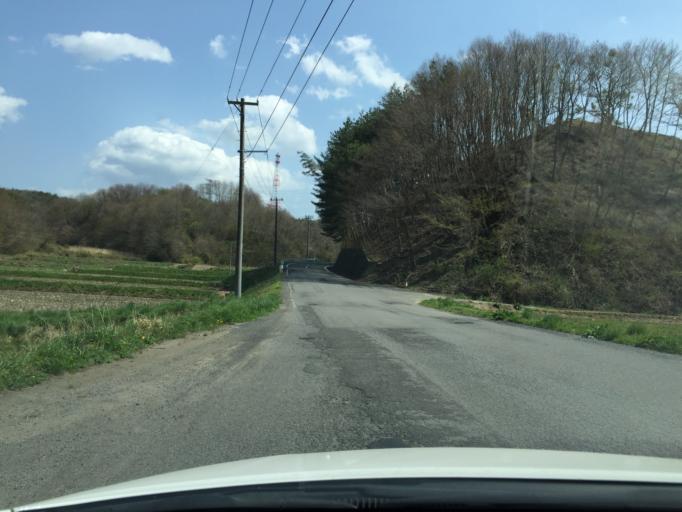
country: JP
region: Fukushima
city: Namie
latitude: 37.3895
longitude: 140.7978
